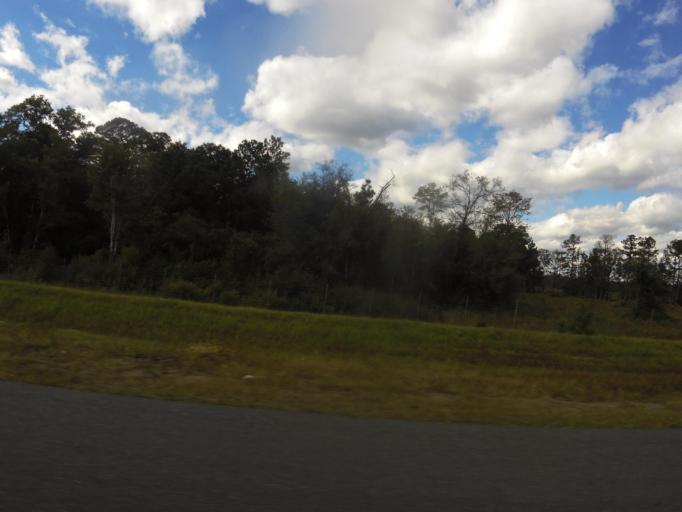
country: US
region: Florida
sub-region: Bradford County
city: Starke
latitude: 29.9558
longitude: -82.1367
